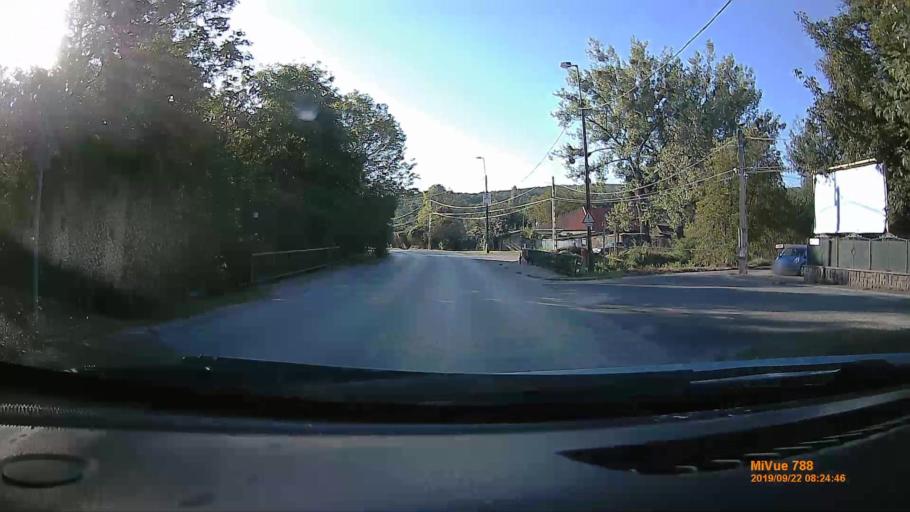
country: HU
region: Borsod-Abauj-Zemplen
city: Miskolc
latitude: 48.0893
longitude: 20.7131
